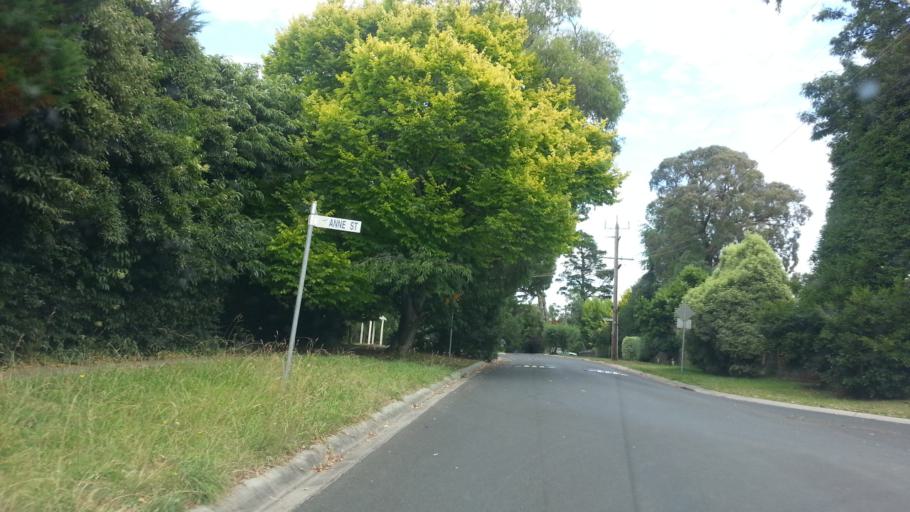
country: AU
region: Victoria
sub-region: Cardinia
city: Emerald
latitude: -37.9334
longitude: 145.4358
